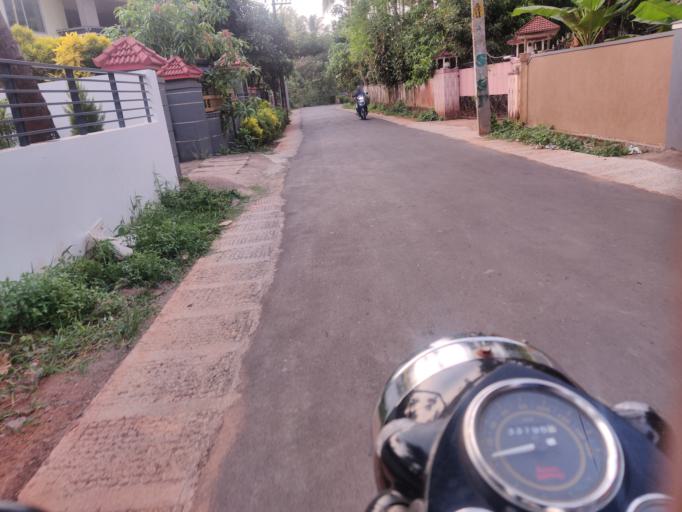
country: IN
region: Kerala
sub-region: Kozhikode
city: Mavoor
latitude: 11.2629
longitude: 75.9502
